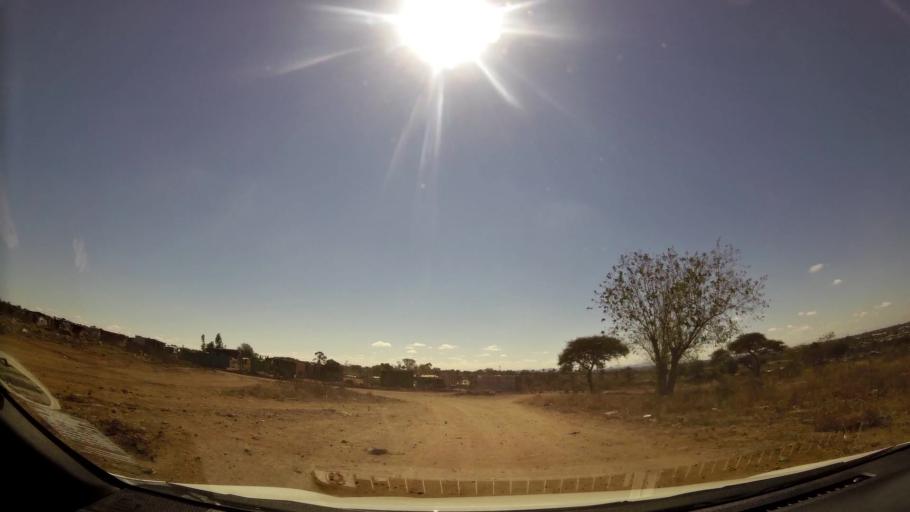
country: ZA
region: Limpopo
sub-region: Capricorn District Municipality
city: Polokwane
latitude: -23.8786
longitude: 29.4252
